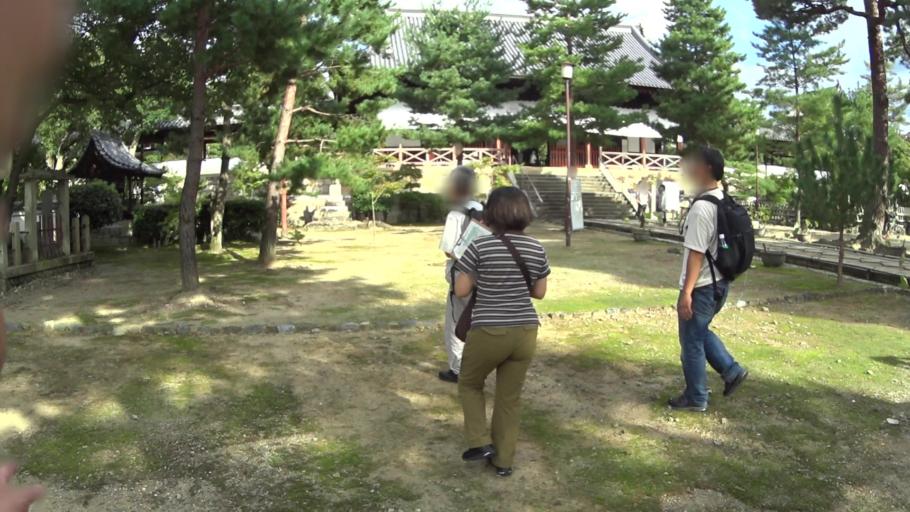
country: JP
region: Kyoto
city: Uji
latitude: 34.9139
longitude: 135.8066
